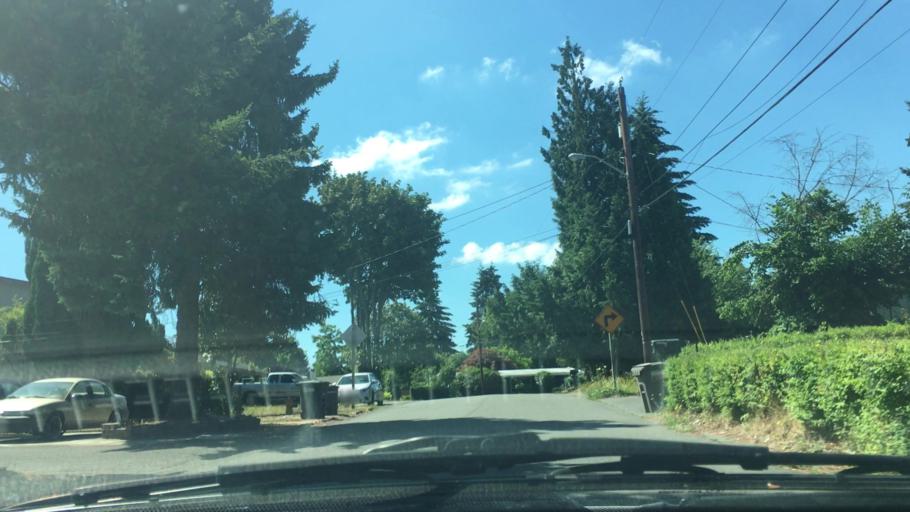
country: US
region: Washington
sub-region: King County
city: SeaTac
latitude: 47.4373
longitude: -122.2859
